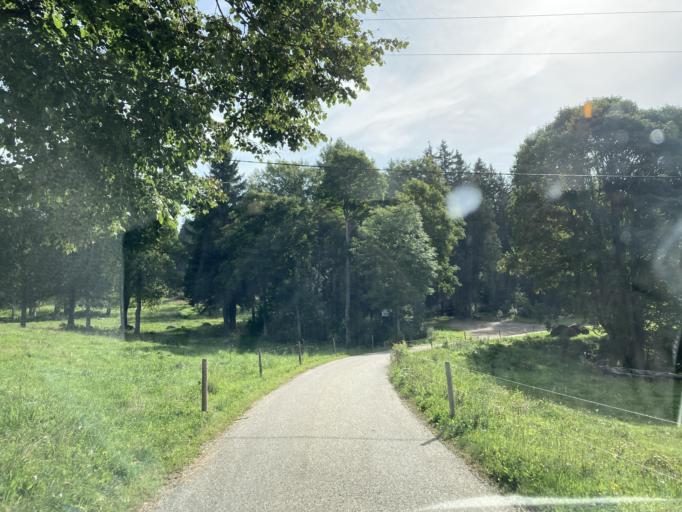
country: DE
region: Baden-Wuerttemberg
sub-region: Freiburg Region
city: Schonwald im Schwarzwald
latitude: 48.0958
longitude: 8.2239
